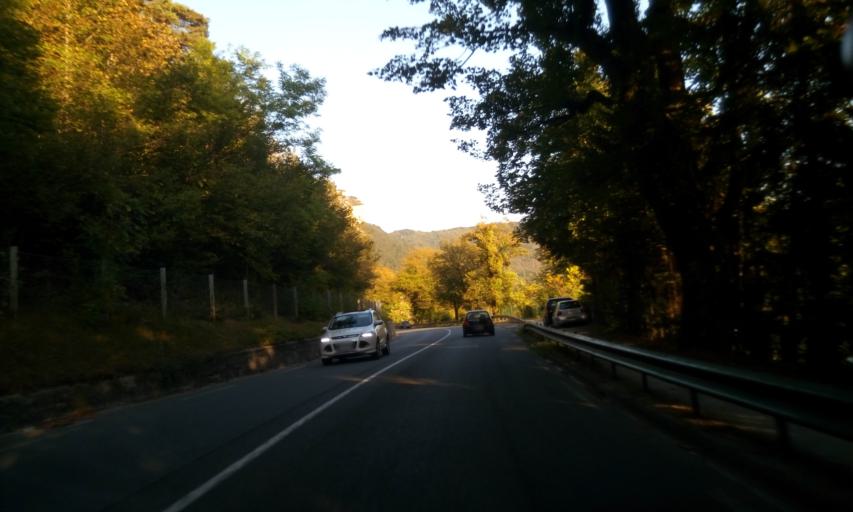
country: FR
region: Rhone-Alpes
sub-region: Departement de l'Ain
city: Montreal-la-Cluse
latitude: 46.1641
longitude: 5.5877
